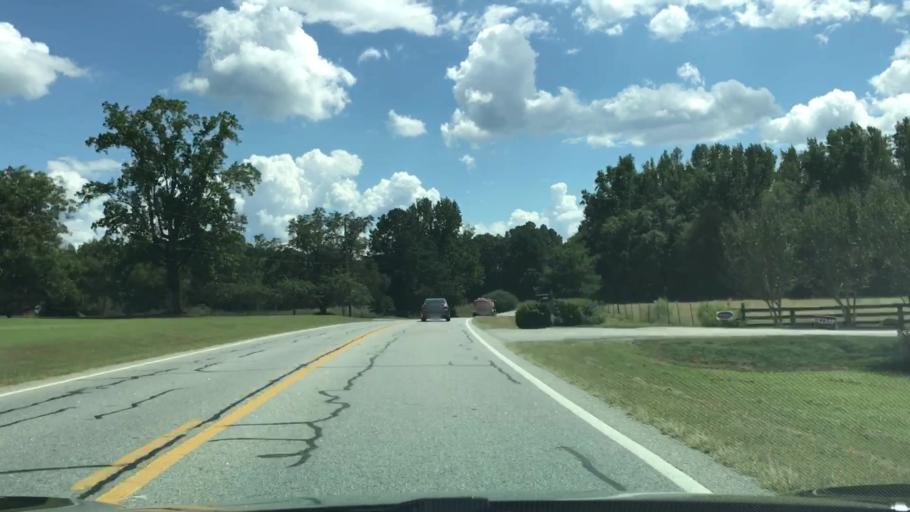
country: US
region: Georgia
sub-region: Oconee County
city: Watkinsville
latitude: 33.7520
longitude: -83.3023
